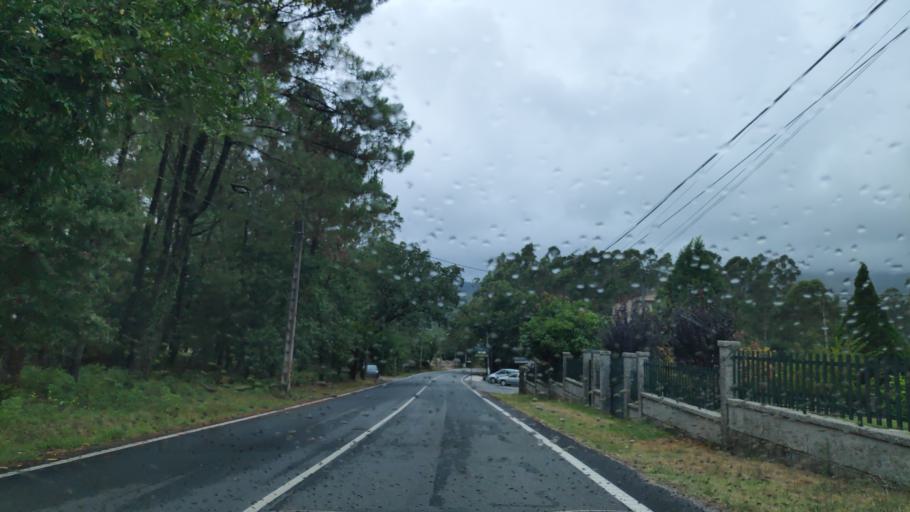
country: ES
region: Galicia
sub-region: Provincia de Pontevedra
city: Catoira
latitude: 42.6932
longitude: -8.7742
